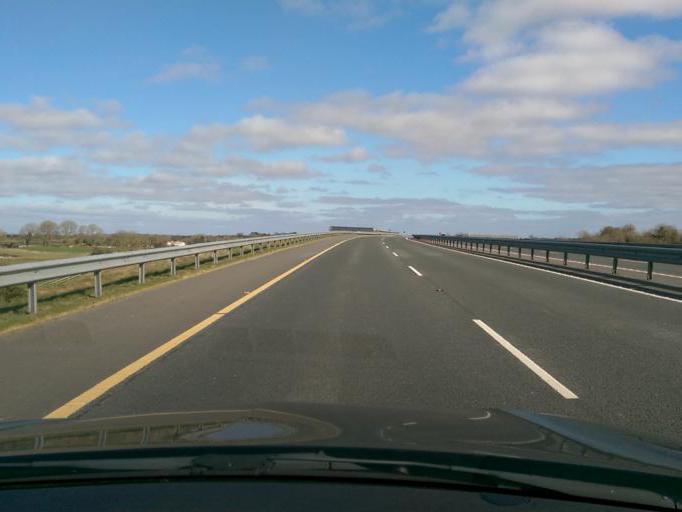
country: IE
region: Leinster
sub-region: An Iarmhi
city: Athlone
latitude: 53.3960
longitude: -8.0487
